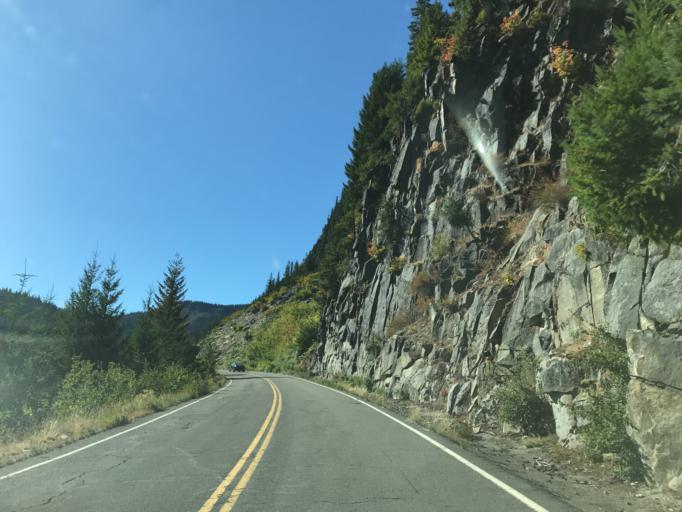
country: US
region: Washington
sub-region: Pierce County
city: Buckley
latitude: 46.7690
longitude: -121.6767
